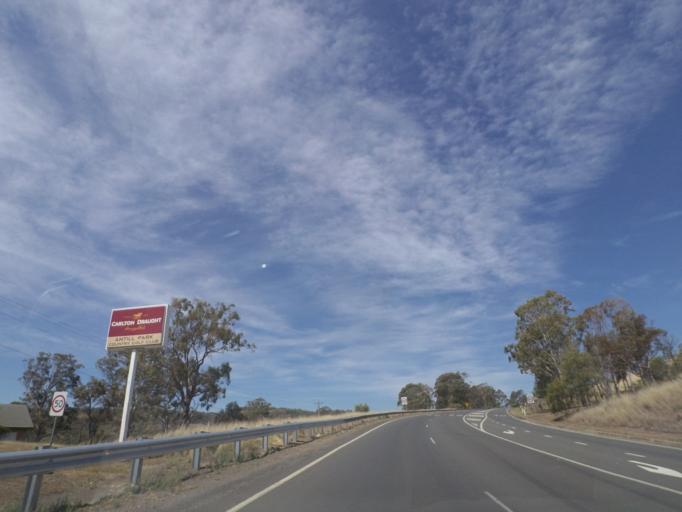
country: AU
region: New South Wales
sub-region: Wollondilly
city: Picton
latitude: -34.1625
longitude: 150.6167
